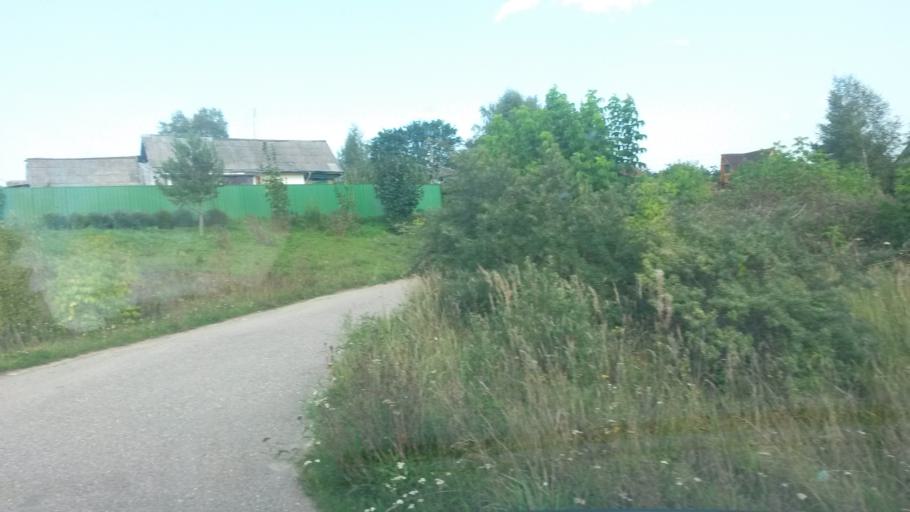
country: RU
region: Vladimir
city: Balakirevo
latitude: 56.6219
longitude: 38.6658
